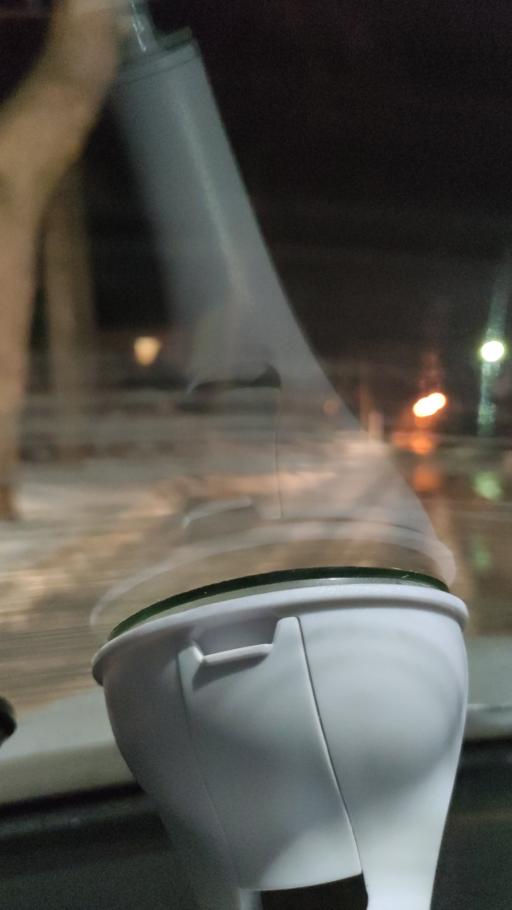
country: RU
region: Samara
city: Samara
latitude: 53.2951
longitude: 50.2021
